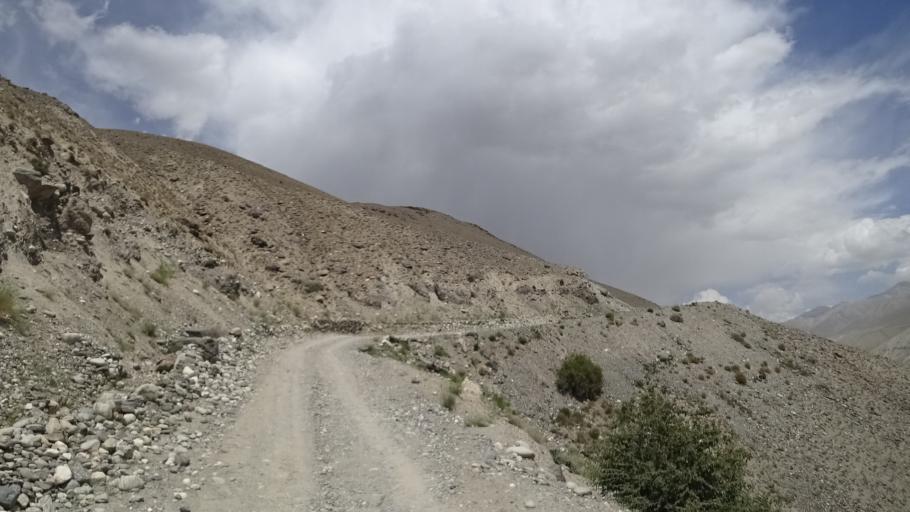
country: AF
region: Badakhshan
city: Khandud
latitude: 37.0851
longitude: 72.7008
